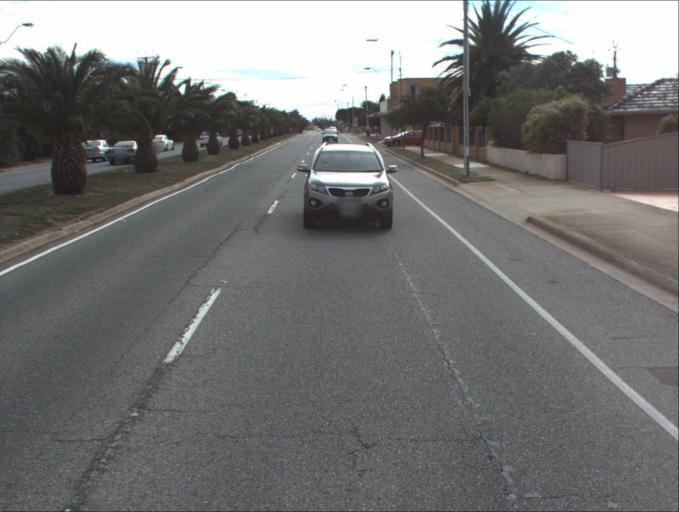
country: AU
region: South Australia
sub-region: Charles Sturt
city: West Lakes Shore
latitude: -34.8616
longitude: 138.4793
